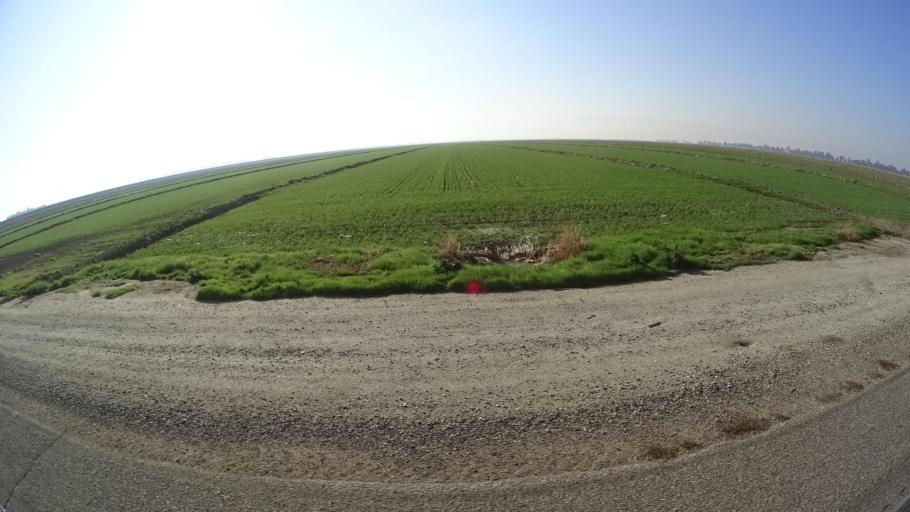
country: US
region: California
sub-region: Kern County
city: Greenfield
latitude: 35.2086
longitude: -118.9805
